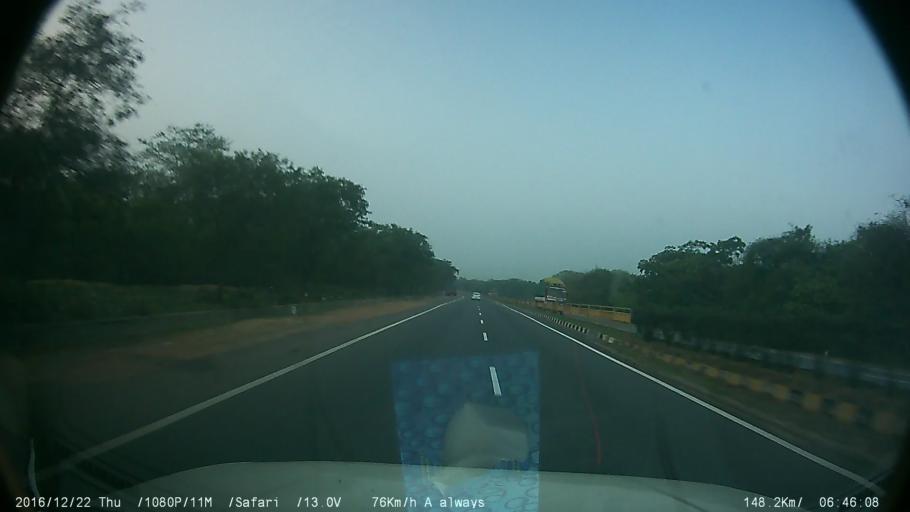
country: IN
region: Tamil Nadu
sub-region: Dharmapuri
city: Dharmapuri
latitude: 11.9908
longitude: 78.0666
